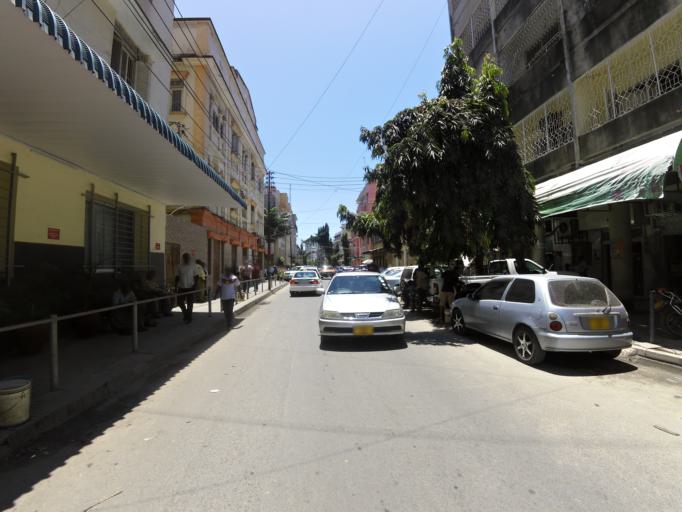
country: TZ
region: Dar es Salaam
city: Dar es Salaam
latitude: -6.8170
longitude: 39.2863
